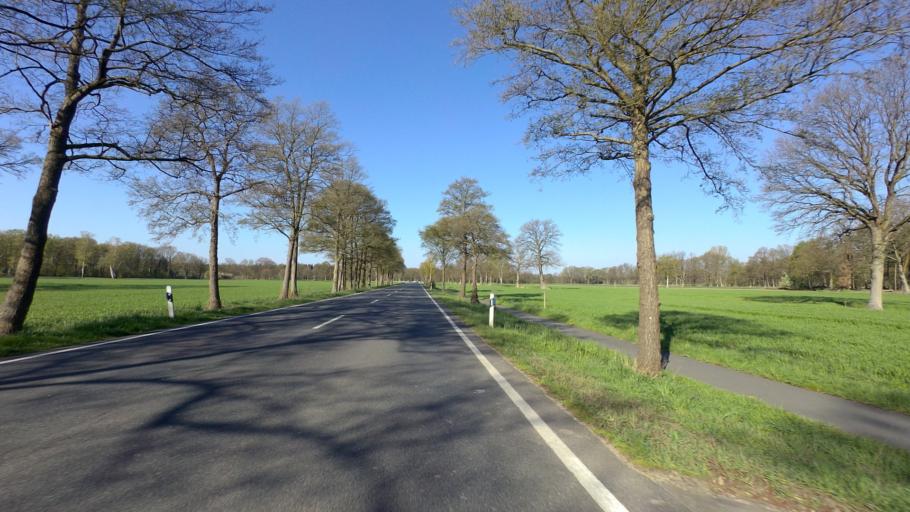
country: DE
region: Lower Saxony
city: Steimbke
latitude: 52.6594
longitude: 9.4621
